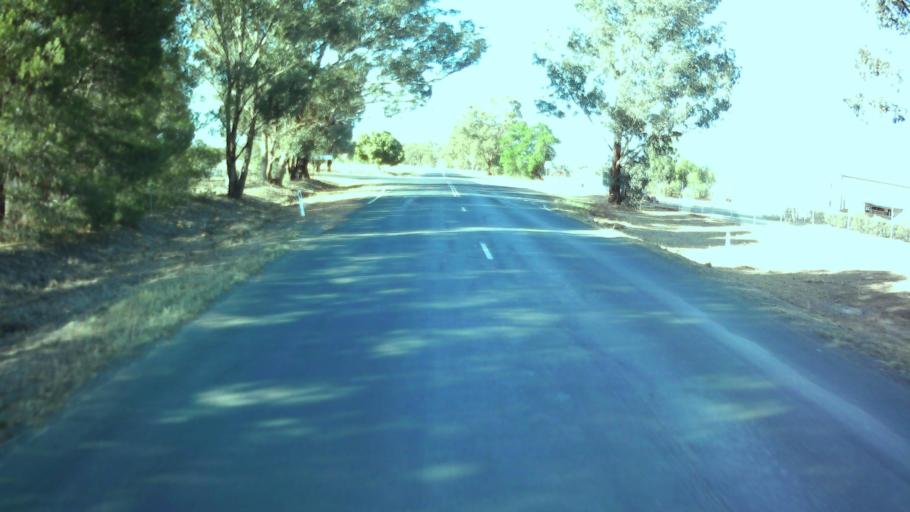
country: AU
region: New South Wales
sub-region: Weddin
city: Grenfell
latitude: -33.9050
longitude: 148.1483
